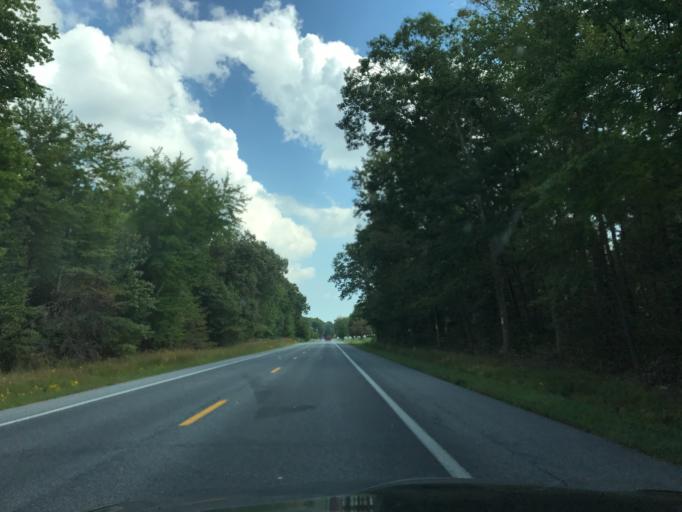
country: US
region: Delaware
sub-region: Kent County
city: Clayton
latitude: 39.1957
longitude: -75.7967
